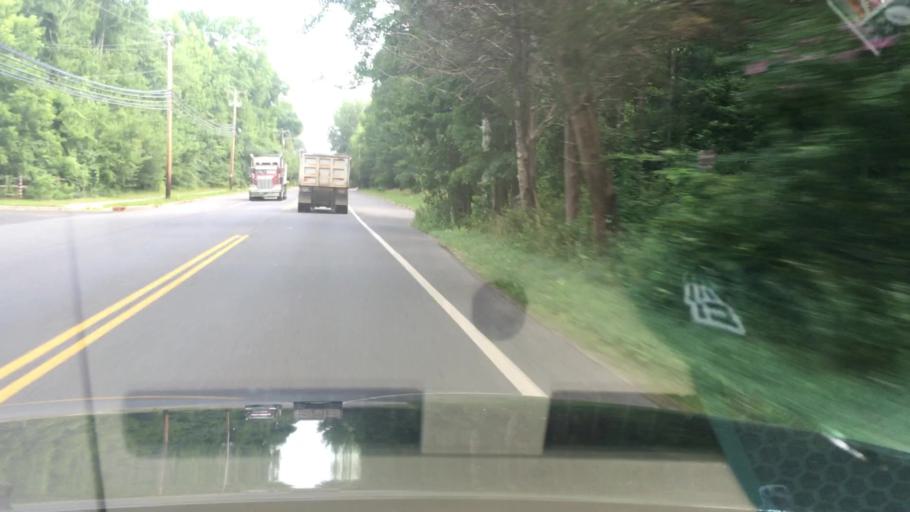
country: US
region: New Jersey
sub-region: Ocean County
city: Vista Center
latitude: 40.1437
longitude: -74.3970
